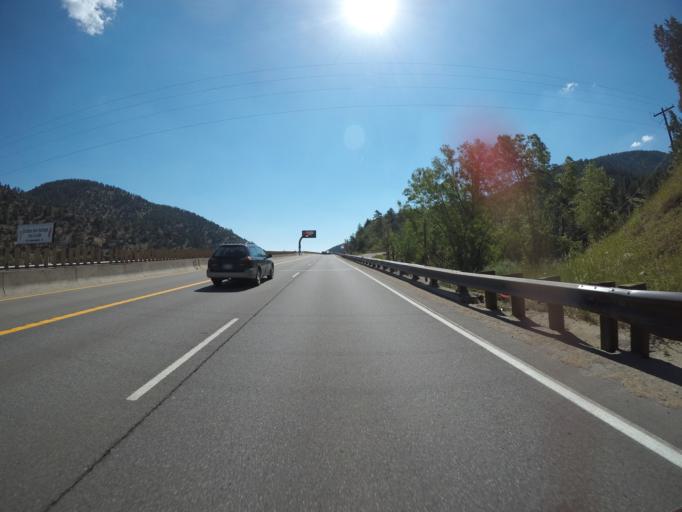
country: US
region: Colorado
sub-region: Clear Creek County
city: Idaho Springs
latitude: 39.7413
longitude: -105.5126
